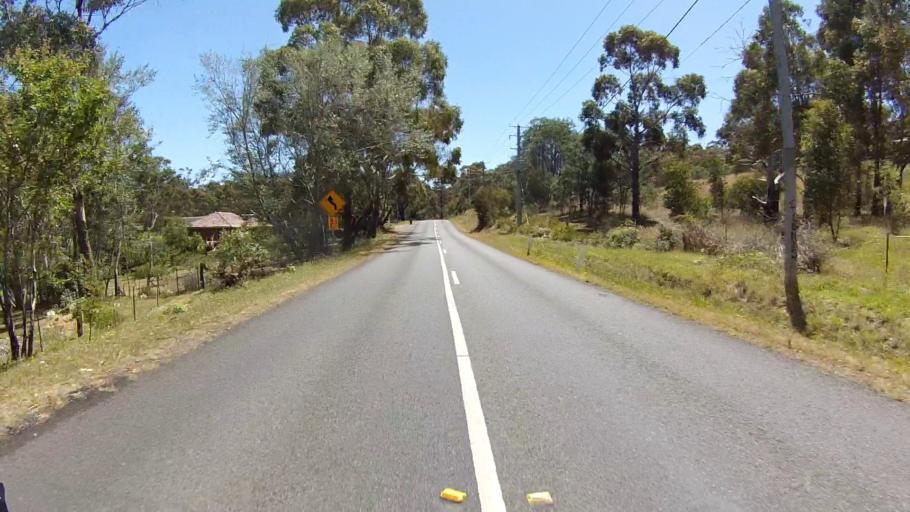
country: AU
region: Tasmania
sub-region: Clarence
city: Howrah
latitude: -42.8671
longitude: 147.4242
